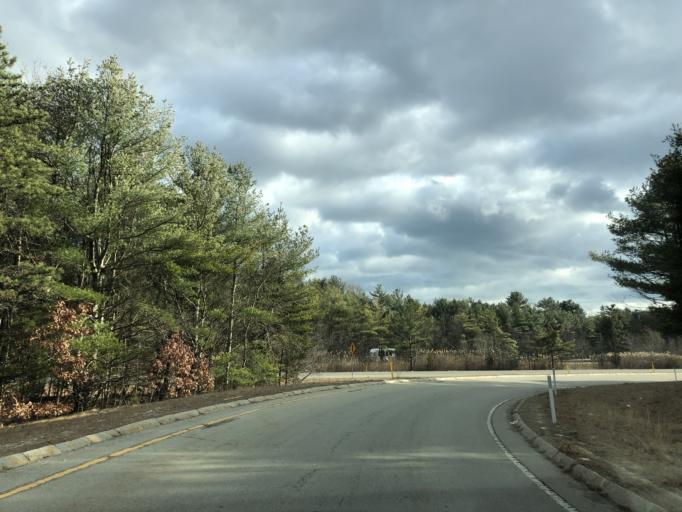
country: US
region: Massachusetts
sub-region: Plymouth County
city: Marion Center
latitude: 41.7270
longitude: -70.7743
